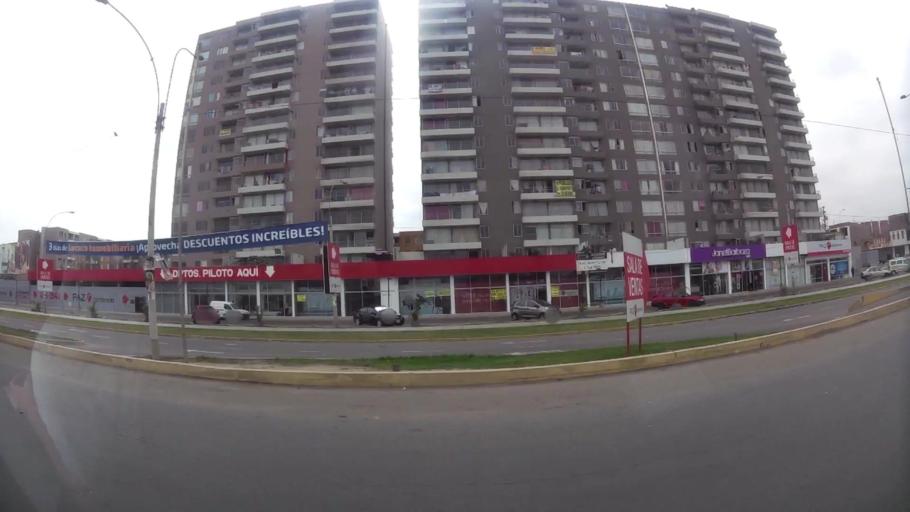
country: PE
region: Callao
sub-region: Callao
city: Callao
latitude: -11.9977
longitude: -77.1137
